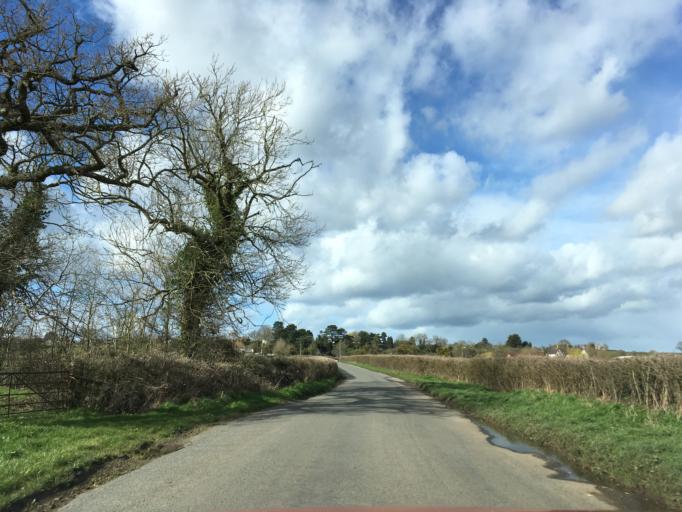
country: GB
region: England
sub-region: Gloucestershire
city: Newent
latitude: 51.8393
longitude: -2.3970
